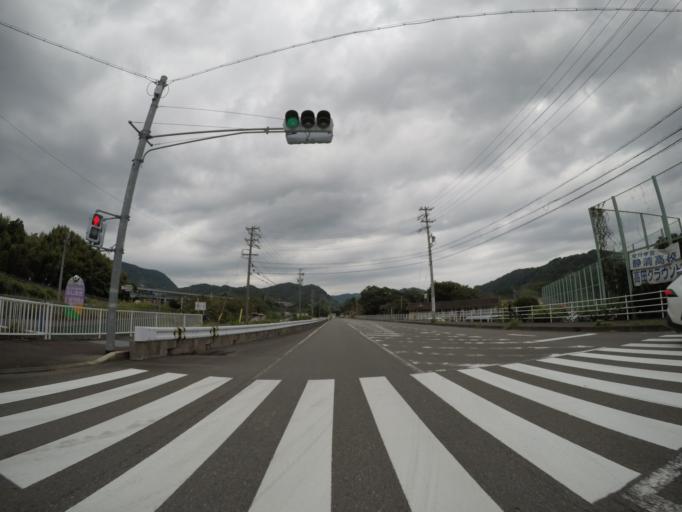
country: JP
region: Shizuoka
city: Fujieda
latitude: 34.9105
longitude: 138.2638
